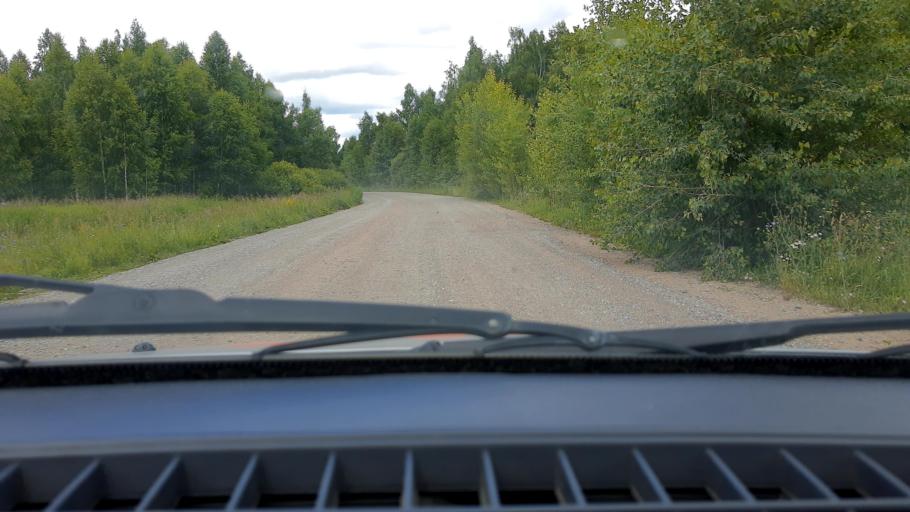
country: RU
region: Bashkortostan
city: Ufa
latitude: 54.6678
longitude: 56.0773
